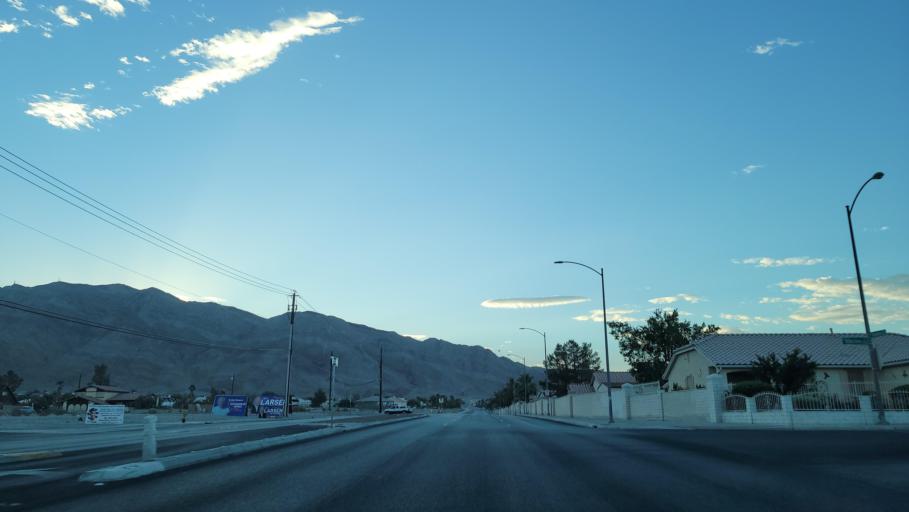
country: US
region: Nevada
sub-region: Clark County
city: Sunrise Manor
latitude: 36.1594
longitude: -115.0347
